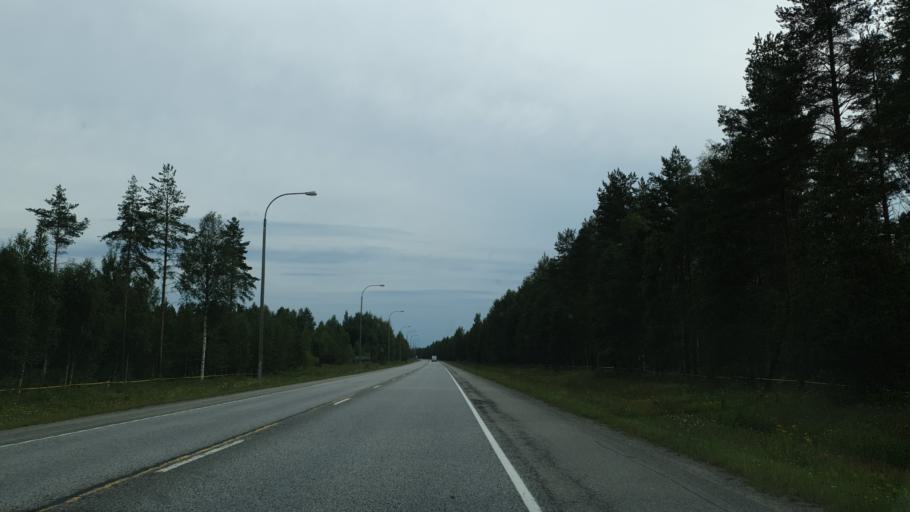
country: FI
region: North Karelia
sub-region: Joensuu
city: Joensuu
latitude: 62.6672
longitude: 29.7883
